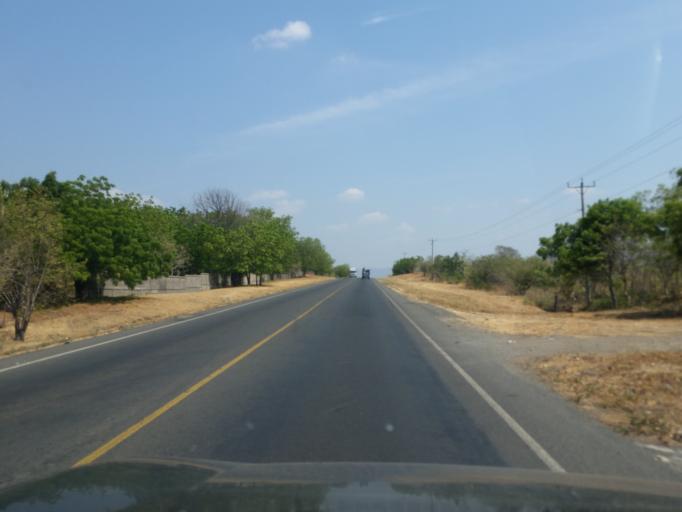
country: NI
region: Managua
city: Tipitapa
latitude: 12.3785
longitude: -86.0459
